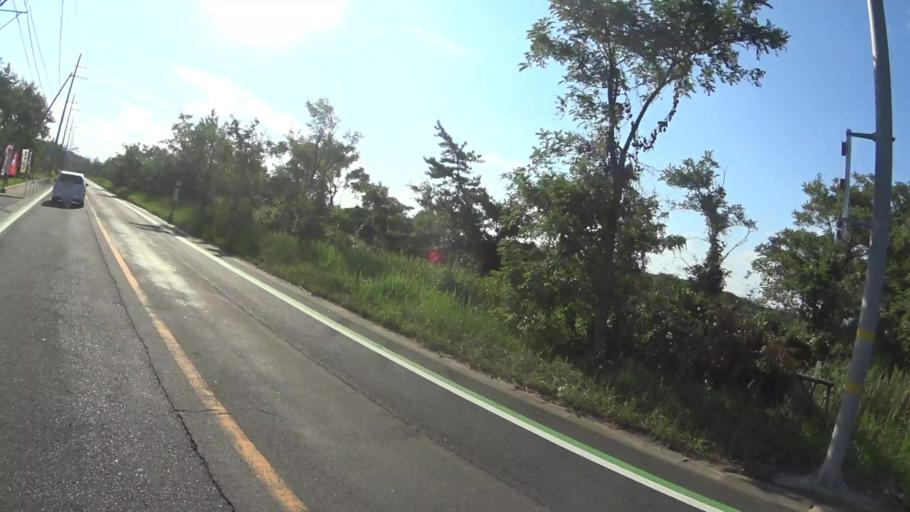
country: JP
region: Hyogo
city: Toyooka
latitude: 35.6588
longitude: 134.9631
